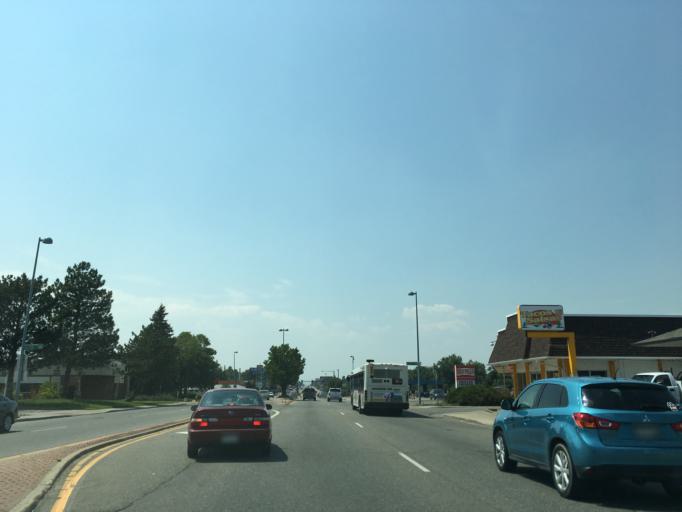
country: US
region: Colorado
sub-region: Adams County
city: Aurora
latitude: 39.7402
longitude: -104.8816
